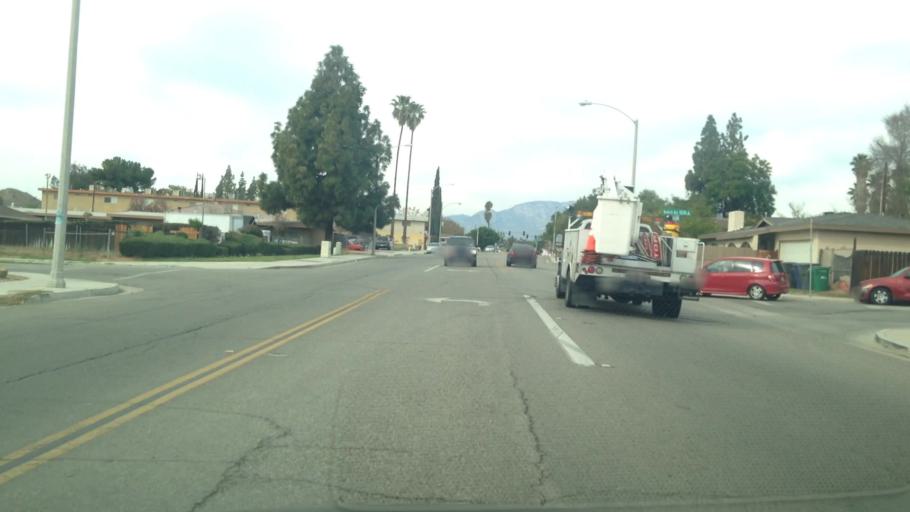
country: US
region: California
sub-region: Riverside County
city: Pedley
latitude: 33.9299
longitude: -117.4753
